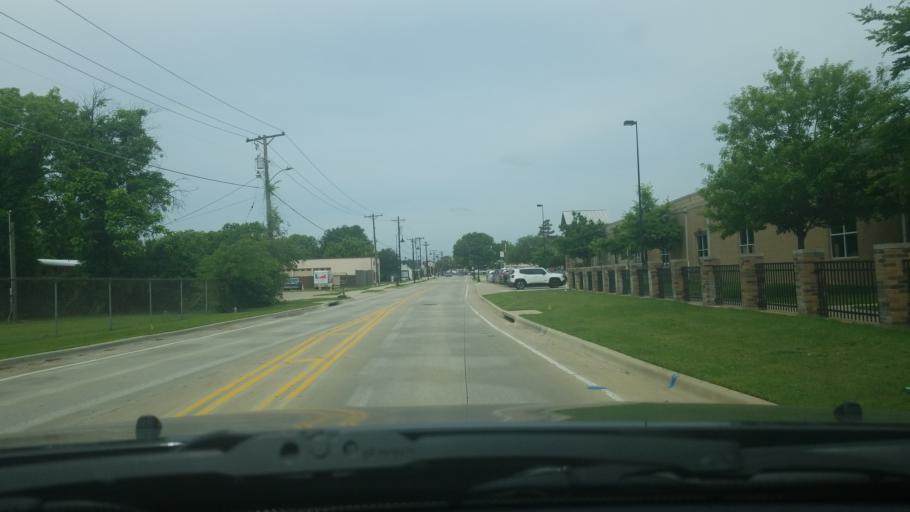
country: US
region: Texas
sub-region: Denton County
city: Lake Dallas
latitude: 33.1193
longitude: -97.0245
